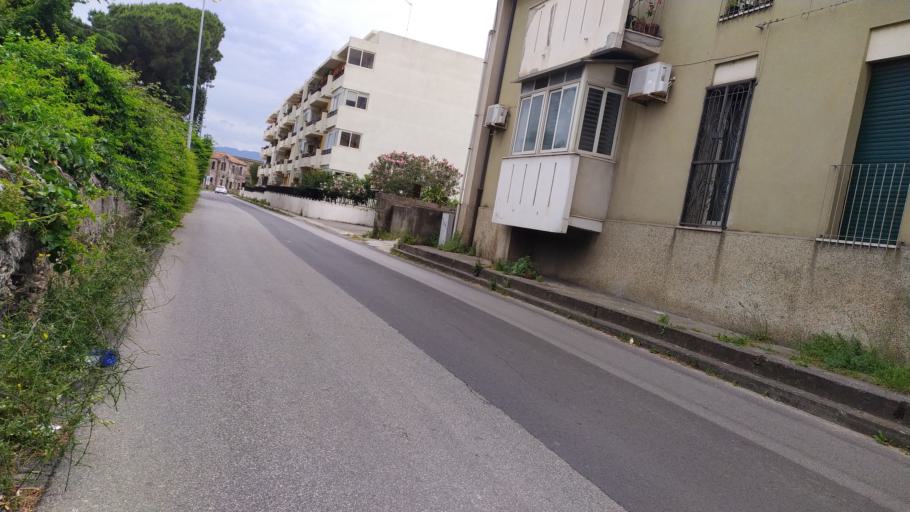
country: IT
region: Sicily
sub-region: Messina
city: Milazzo
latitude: 38.2121
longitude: 15.2429
